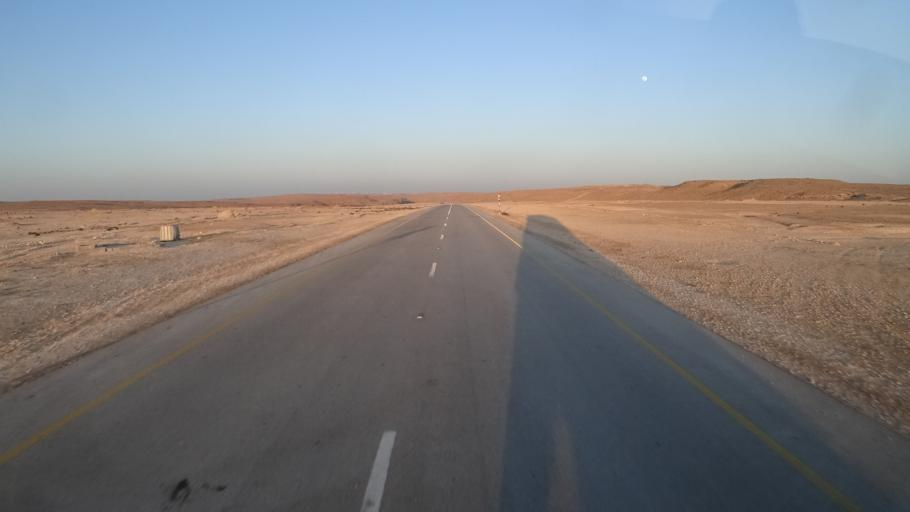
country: YE
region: Al Mahrah
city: Hawf
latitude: 16.9483
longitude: 53.3177
